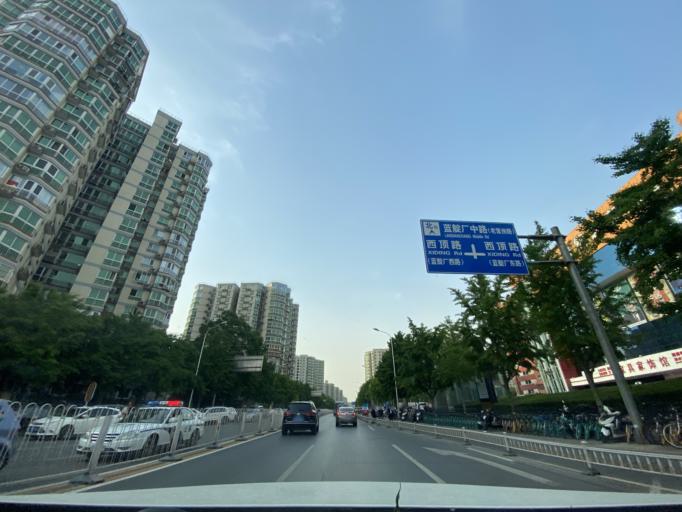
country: CN
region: Beijing
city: Sijiqing
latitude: 39.9567
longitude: 116.2784
